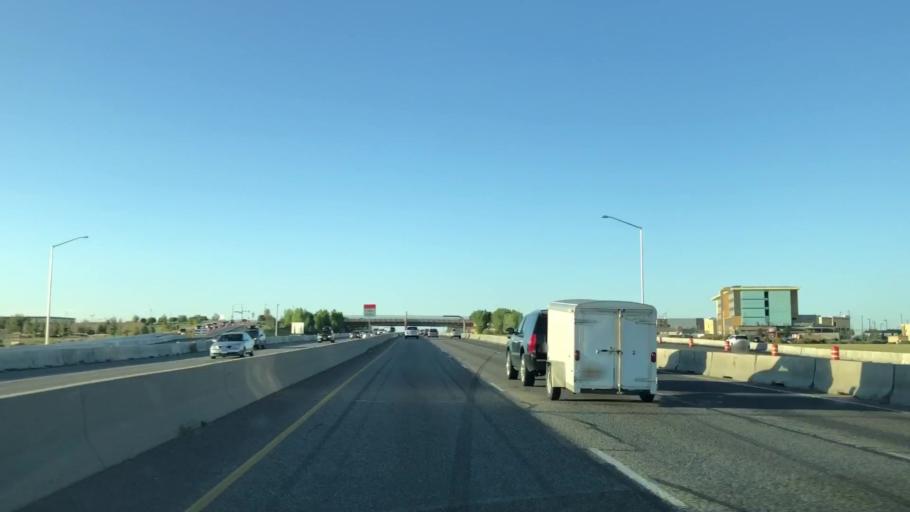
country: US
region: Colorado
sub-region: Adams County
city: Northglenn
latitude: 39.9518
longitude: -104.9885
